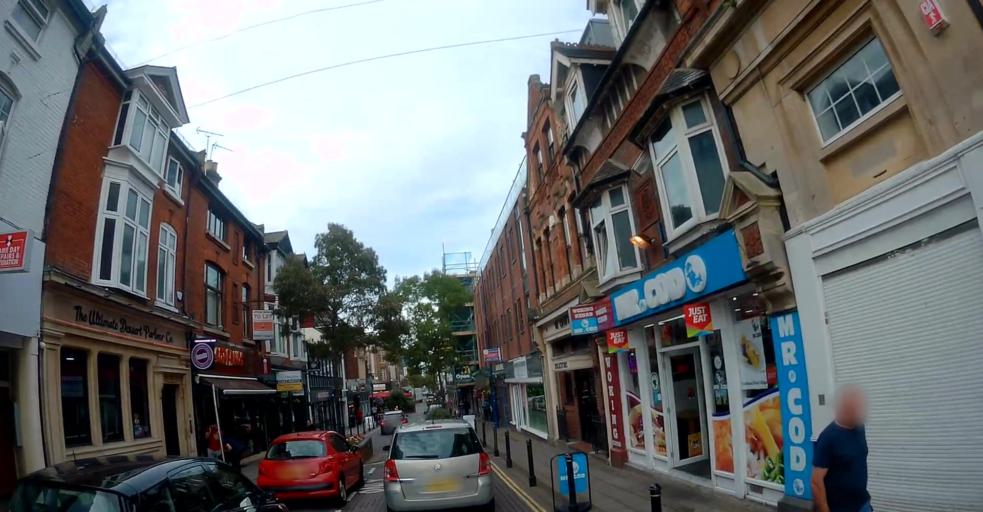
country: GB
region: England
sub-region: Surrey
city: Woking
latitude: 51.3191
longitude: -0.5567
